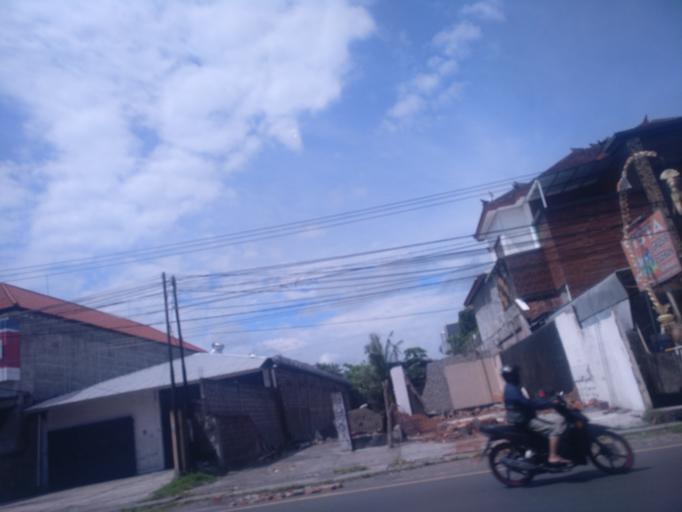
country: ID
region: Bali
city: Banjar Kertasari
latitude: -8.6364
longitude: 115.1908
